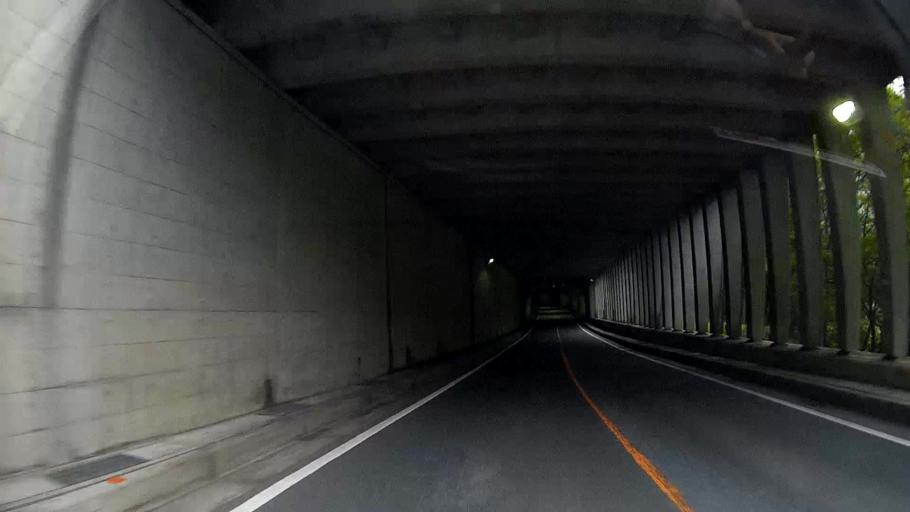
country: JP
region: Yamanashi
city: Enzan
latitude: 35.9136
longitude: 138.8271
